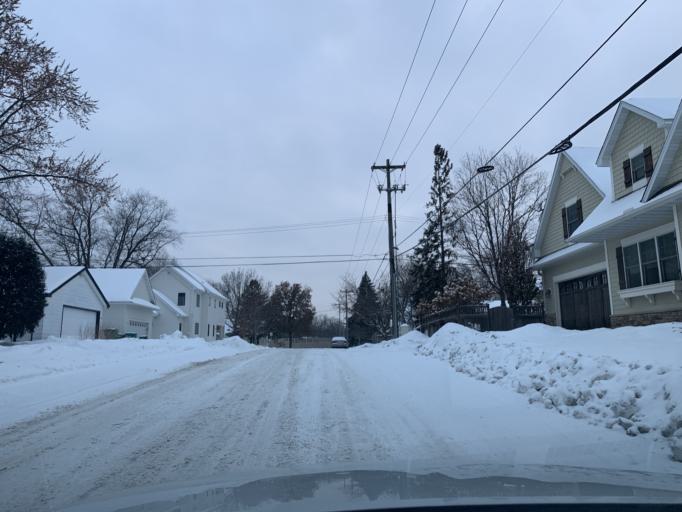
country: US
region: Minnesota
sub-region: Hennepin County
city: Saint Louis Park
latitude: 44.9273
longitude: -93.3472
